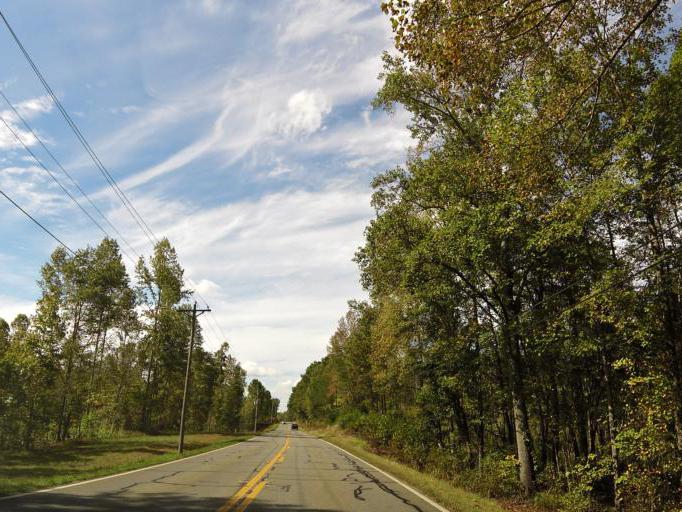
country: US
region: Georgia
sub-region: Pickens County
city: Nelson
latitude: 34.4148
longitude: -84.2970
